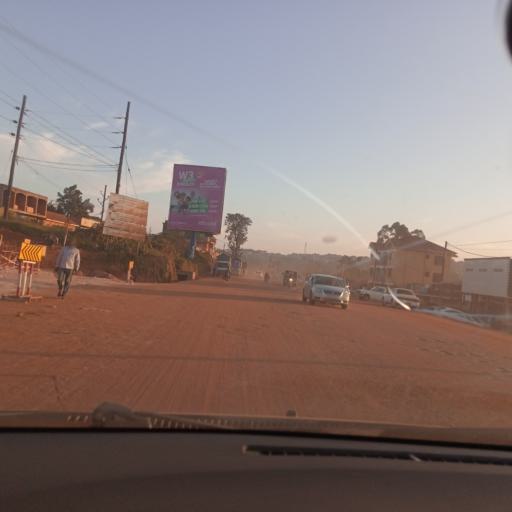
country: UG
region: Central Region
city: Masaka
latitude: -0.3243
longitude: 31.7543
